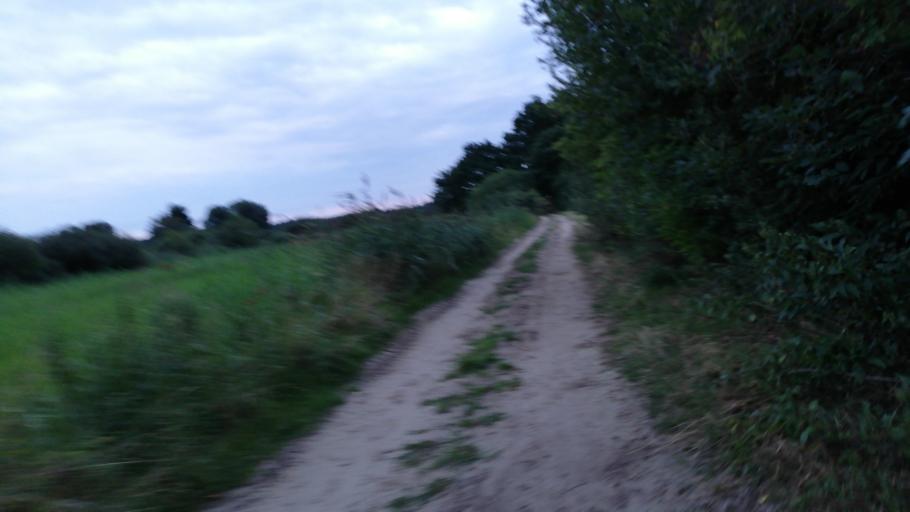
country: DE
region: Lower Saxony
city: Neu Wulmstorf
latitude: 53.4756
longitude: 9.8091
